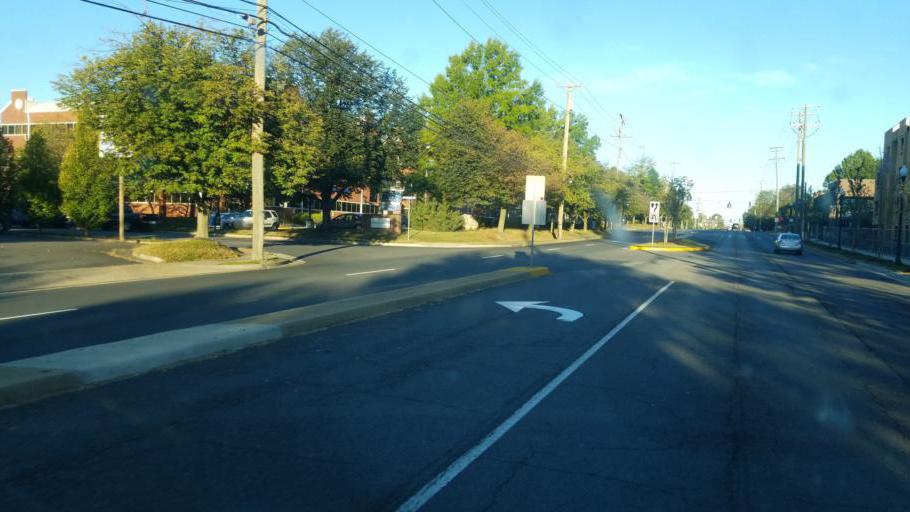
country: US
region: Virginia
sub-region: City of Fairfax
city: Fairfax
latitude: 38.8496
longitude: -77.3164
